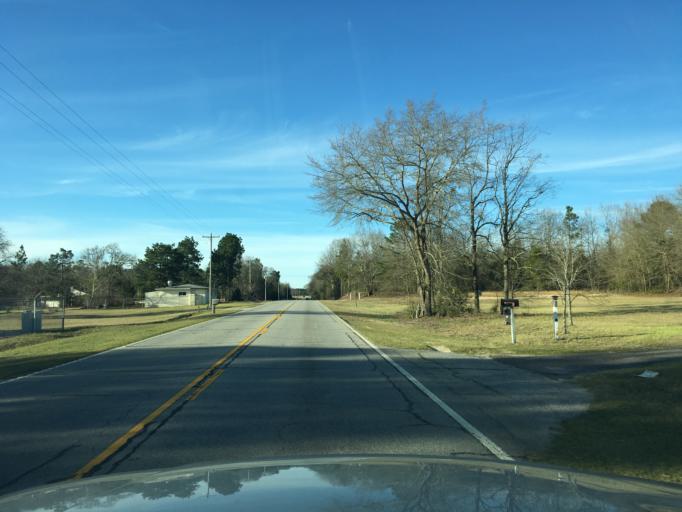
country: US
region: South Carolina
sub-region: Lexington County
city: Batesburg
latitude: 33.7811
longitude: -81.6421
